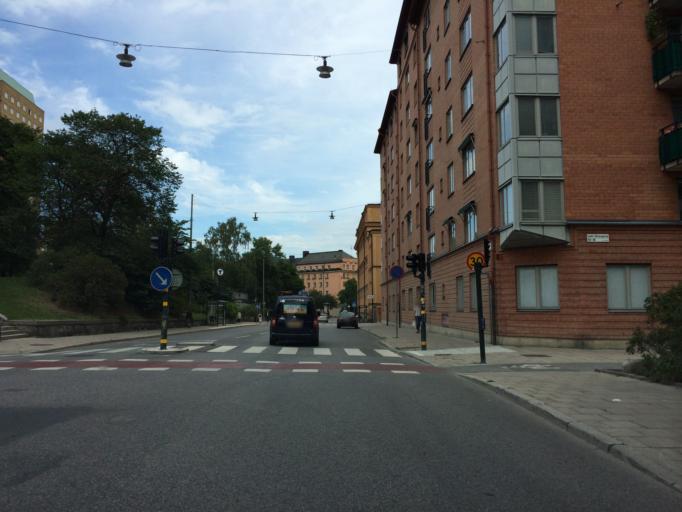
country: SE
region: Stockholm
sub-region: Solna Kommun
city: Solna
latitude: 59.3342
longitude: 18.0250
